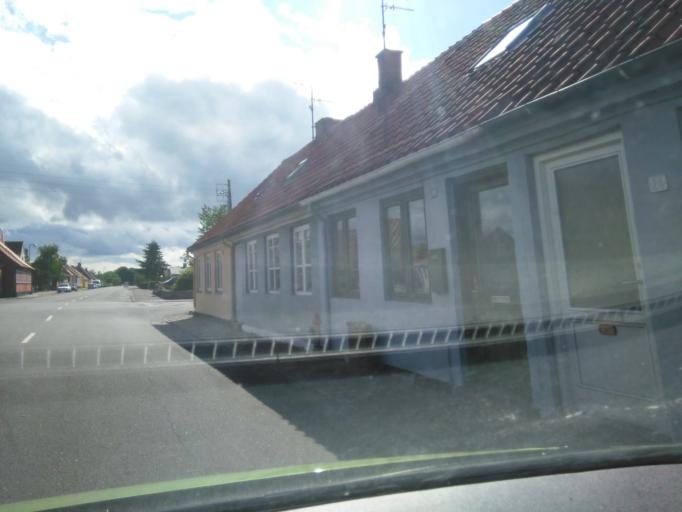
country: DK
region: Capital Region
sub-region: Bornholm Kommune
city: Nexo
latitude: 55.0605
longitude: 15.1271
